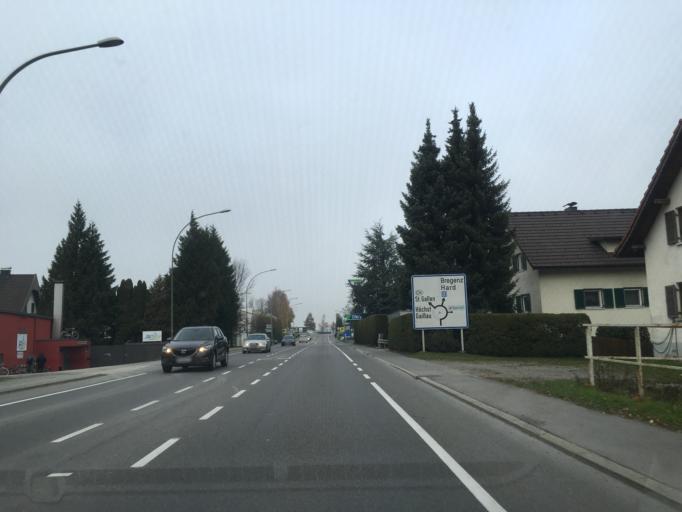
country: AT
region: Vorarlberg
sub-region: Politischer Bezirk Dornbirn
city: Lustenau
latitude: 47.4482
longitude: 9.6646
